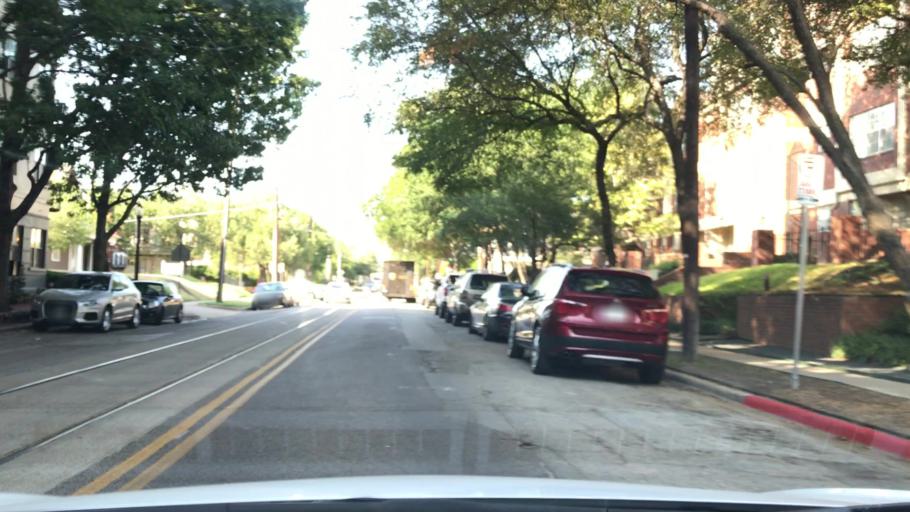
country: US
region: Texas
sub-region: Dallas County
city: Dallas
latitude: 32.8029
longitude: -96.8016
